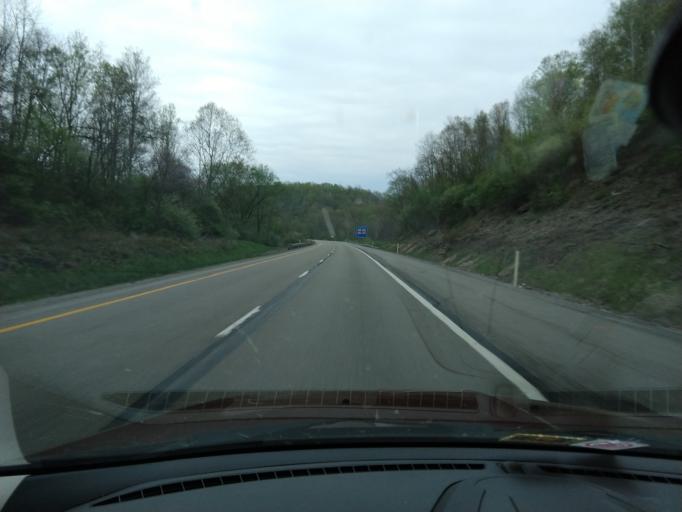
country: US
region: West Virginia
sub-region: Lewis County
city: Weston
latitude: 39.0120
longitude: -80.4553
